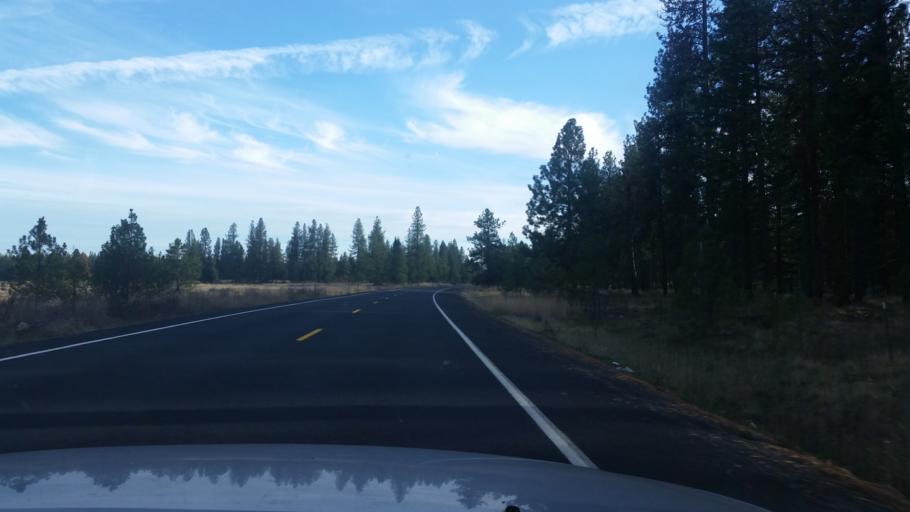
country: US
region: Washington
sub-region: Spokane County
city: Cheney
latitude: 47.4359
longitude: -117.5704
